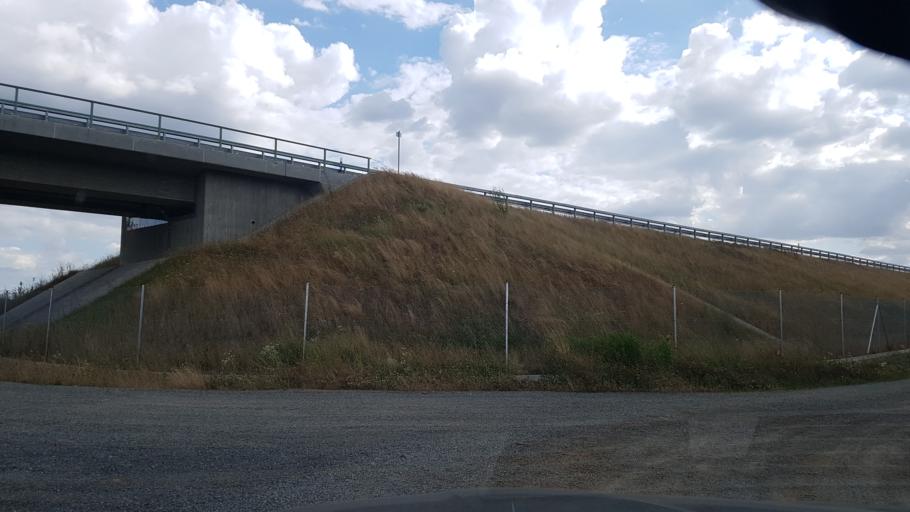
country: DE
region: Brandenburg
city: Bad Liebenwerda
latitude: 51.5057
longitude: 13.4089
